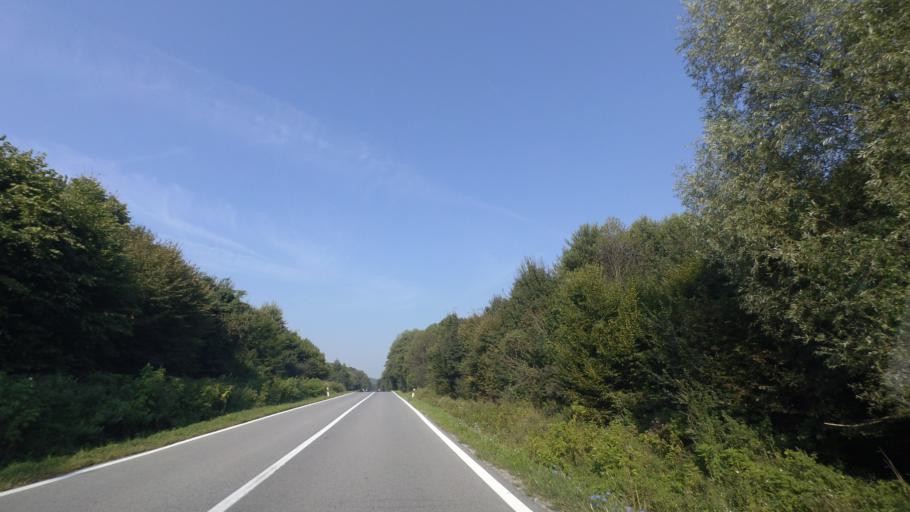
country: HR
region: Bjelovarsko-Bilogorska
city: Sirac
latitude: 45.4682
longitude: 17.3609
